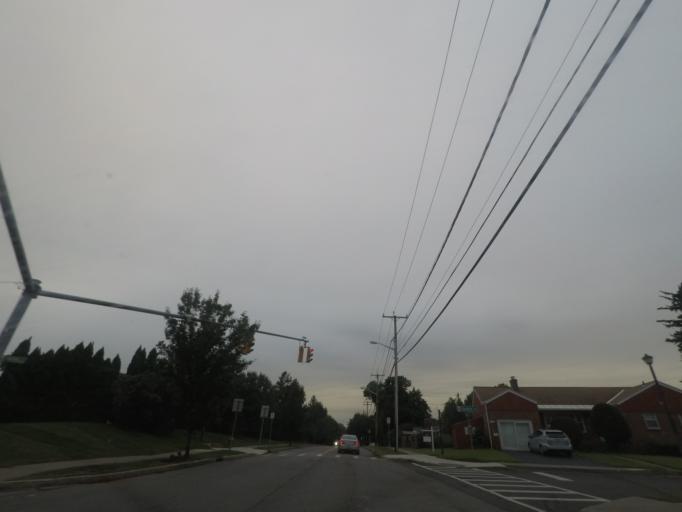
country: US
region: New York
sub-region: Albany County
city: Delmar
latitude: 42.6475
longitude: -73.8017
